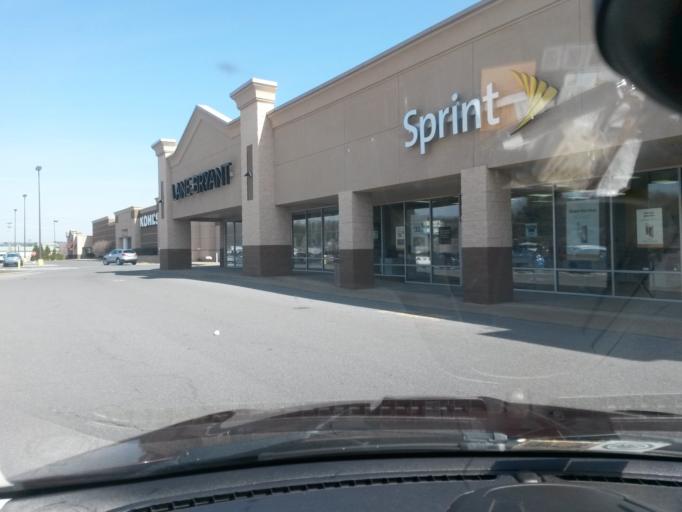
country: US
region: West Virginia
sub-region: Raleigh County
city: Beckley
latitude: 37.8001
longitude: -81.1763
